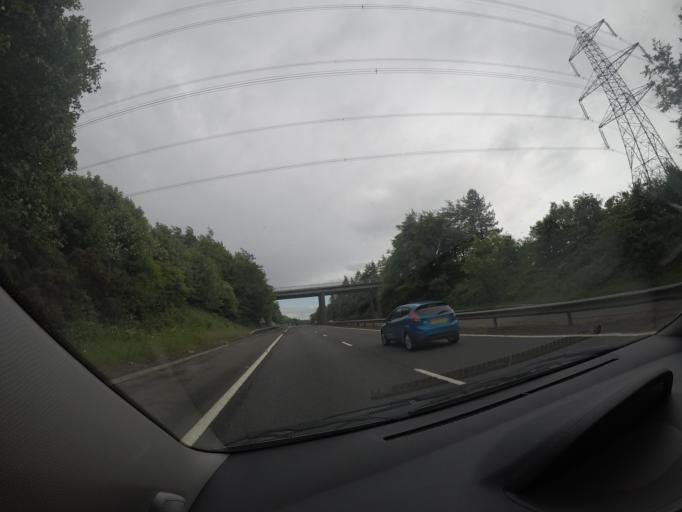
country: GB
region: Scotland
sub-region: Falkirk
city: Denny
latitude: 56.0093
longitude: -3.9188
